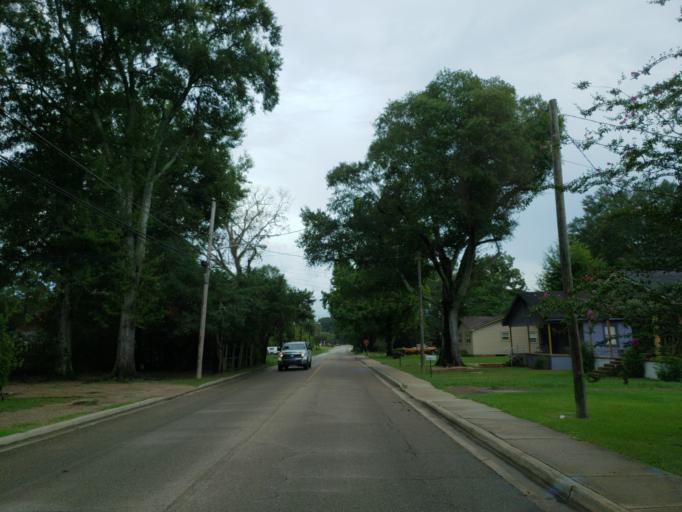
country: US
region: Mississippi
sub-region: Forrest County
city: Hattiesburg
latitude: 31.3149
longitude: -89.2991
